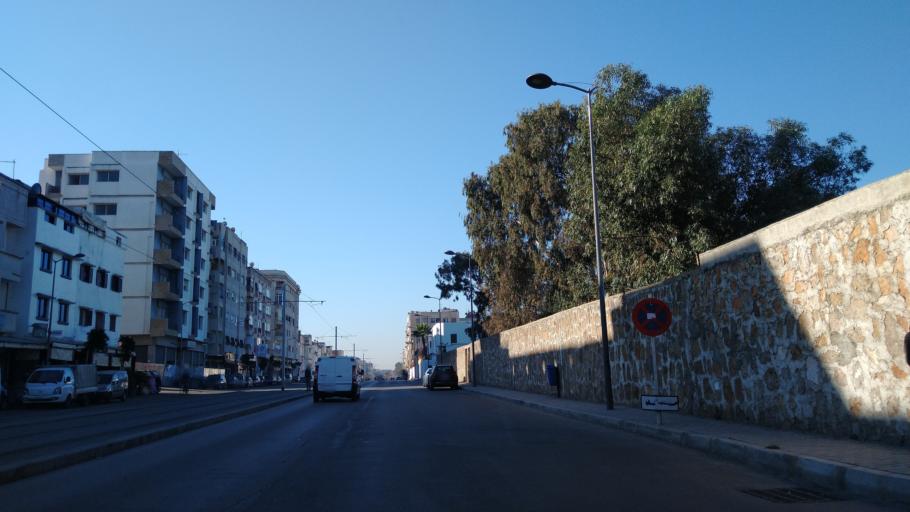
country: MA
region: Rabat-Sale-Zemmour-Zaer
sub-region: Rabat
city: Rabat
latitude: 34.0134
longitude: -6.8571
